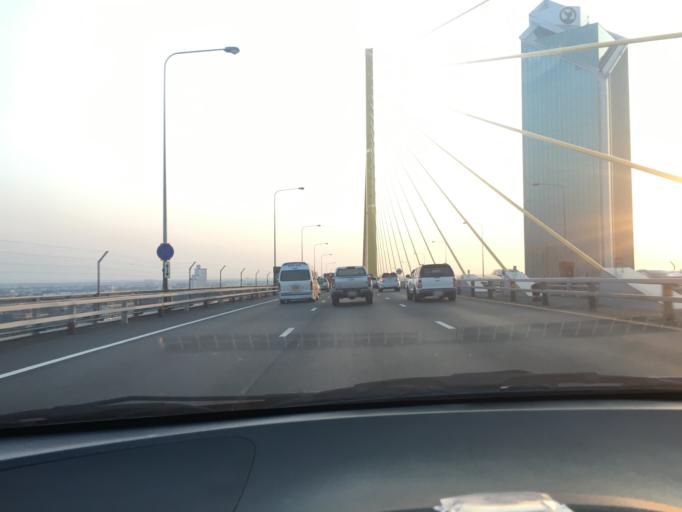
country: TH
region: Bangkok
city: Rat Burana
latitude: 13.6825
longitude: 100.5175
